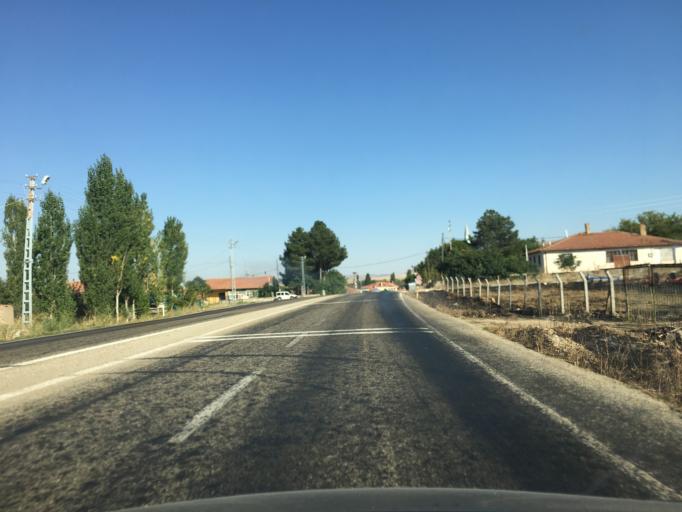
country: TR
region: Kirsehir
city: Akpinar
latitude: 39.3537
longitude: 33.9415
